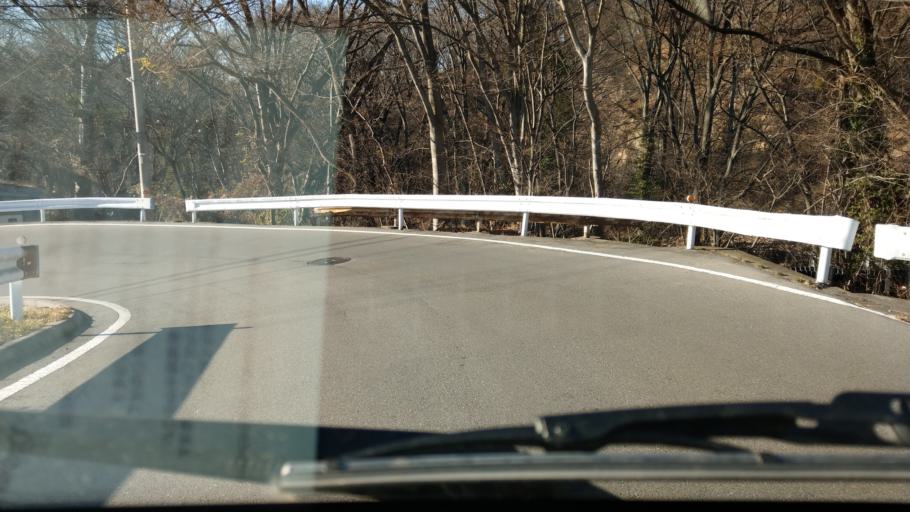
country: JP
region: Nagano
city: Komoro
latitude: 36.3242
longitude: 138.4183
